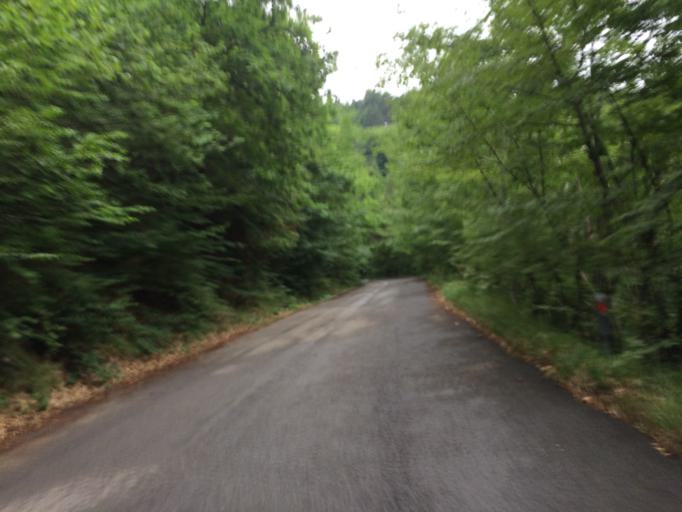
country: IT
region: Liguria
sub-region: Provincia di Imperia
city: Triora
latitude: 43.9763
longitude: 7.7459
